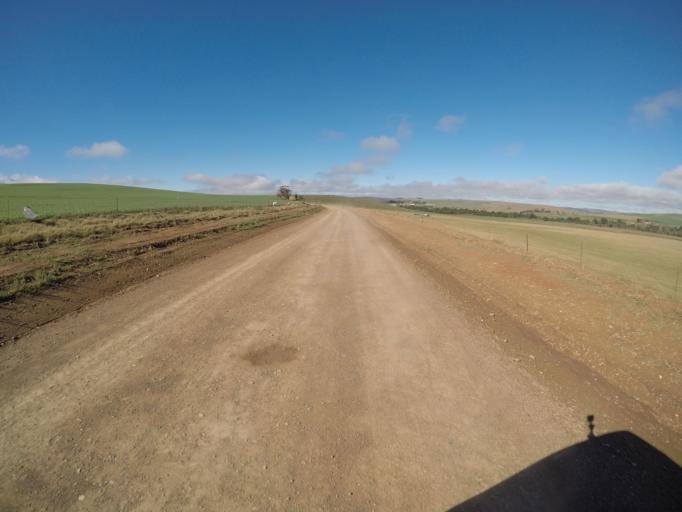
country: ZA
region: Western Cape
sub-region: Overberg District Municipality
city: Caledon
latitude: -34.1170
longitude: 19.7136
